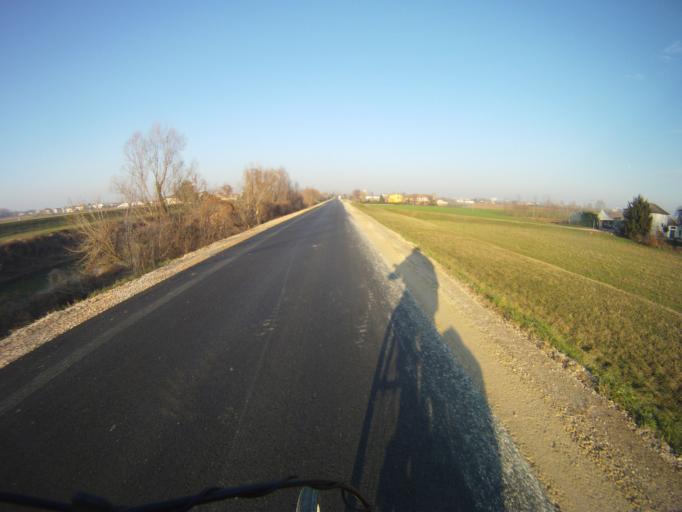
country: IT
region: Veneto
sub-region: Provincia di Padova
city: Legnaro
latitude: 45.3374
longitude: 11.9374
